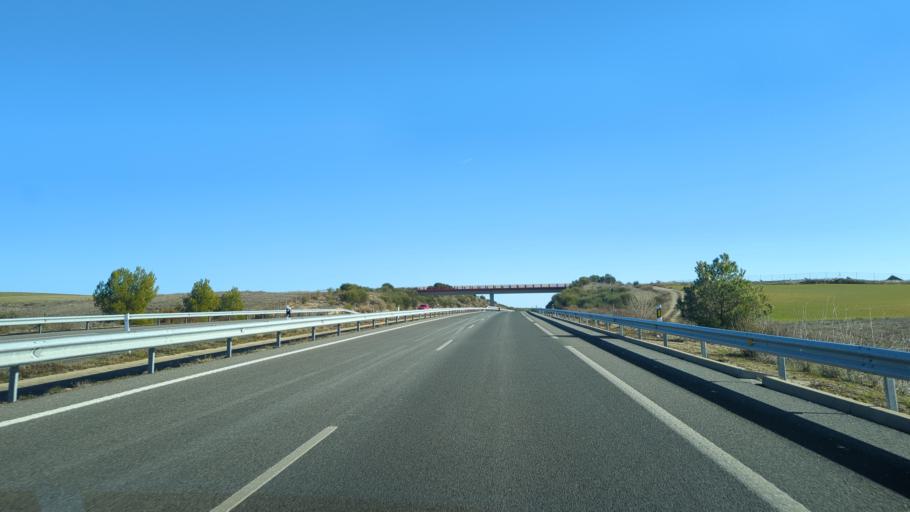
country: ES
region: Navarre
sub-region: Provincia de Navarra
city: Lazagurria
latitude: 42.4974
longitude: -2.2818
